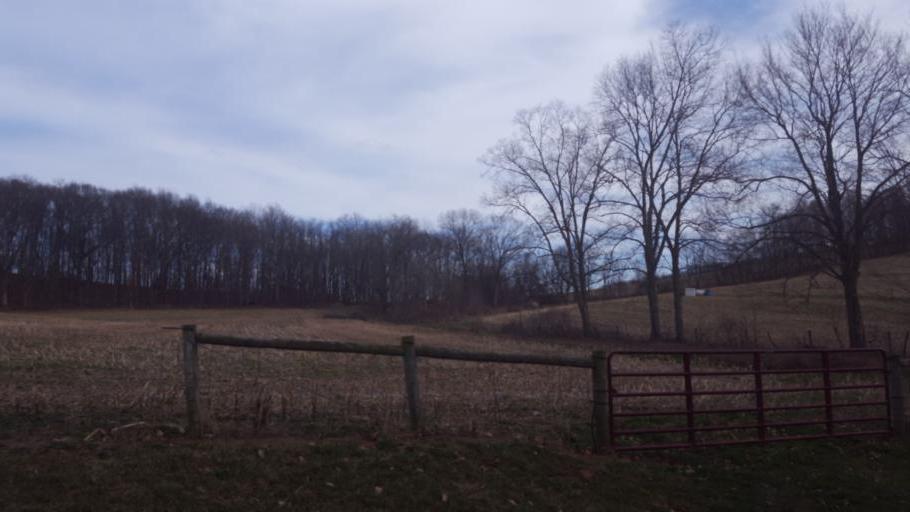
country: US
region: Ohio
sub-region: Knox County
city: Gambier
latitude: 40.4978
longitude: -82.4050
